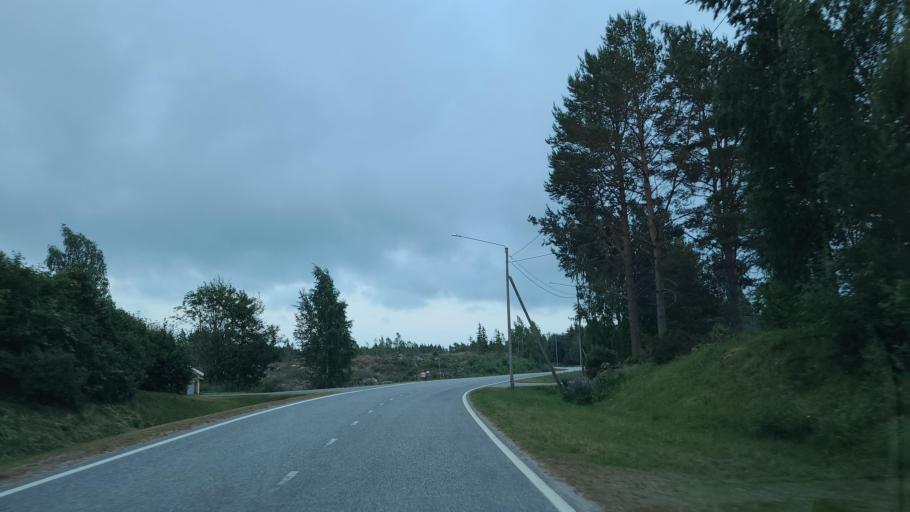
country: FI
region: Ostrobothnia
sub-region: Vaasa
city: Replot
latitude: 63.2834
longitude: 21.1253
